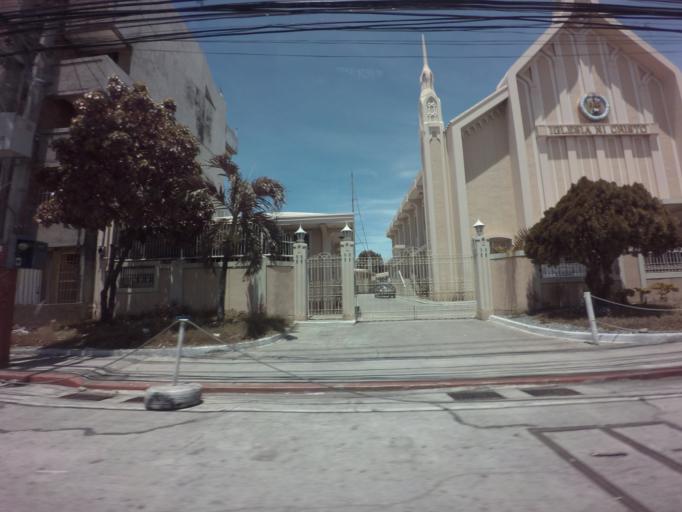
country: PH
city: Sambayanihan People's Village
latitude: 14.4848
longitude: 120.9848
